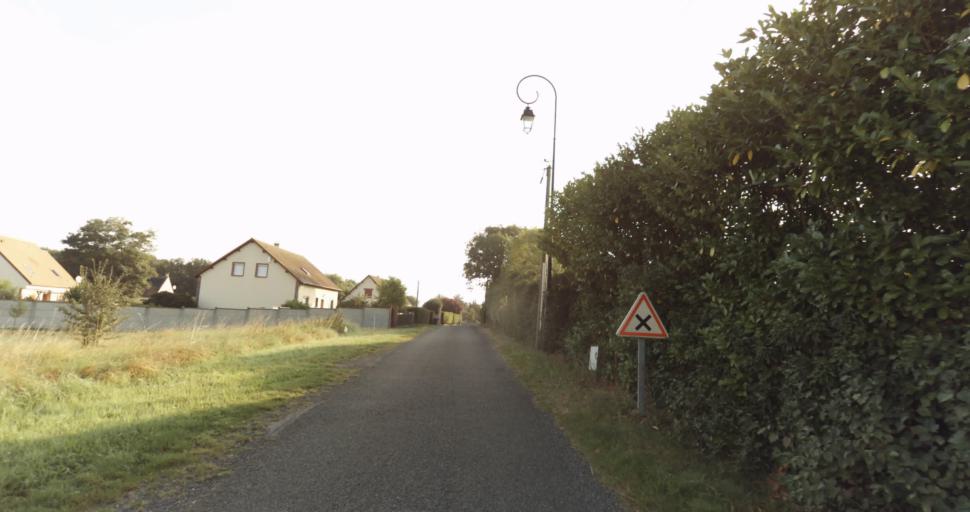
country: FR
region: Haute-Normandie
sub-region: Departement de l'Eure
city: Marcilly-sur-Eure
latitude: 48.7854
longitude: 1.3401
